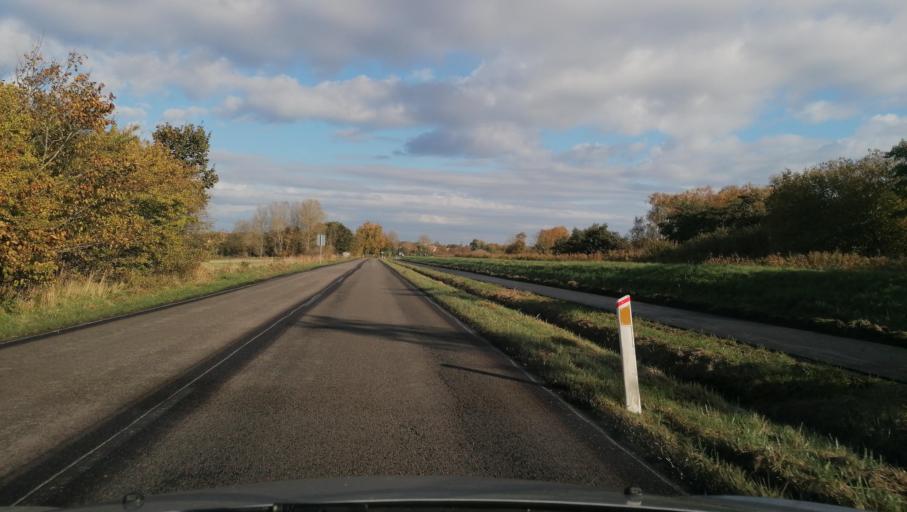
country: DK
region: Zealand
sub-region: Odsherred Kommune
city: Asnaes
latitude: 55.8048
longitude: 11.4839
